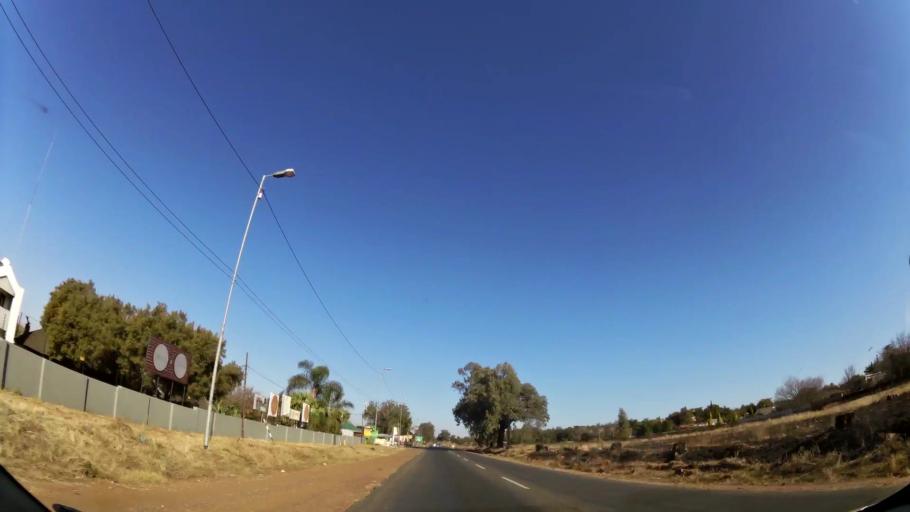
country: ZA
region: Gauteng
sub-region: City of Tshwane Metropolitan Municipality
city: Centurion
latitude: -25.8383
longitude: 28.1619
